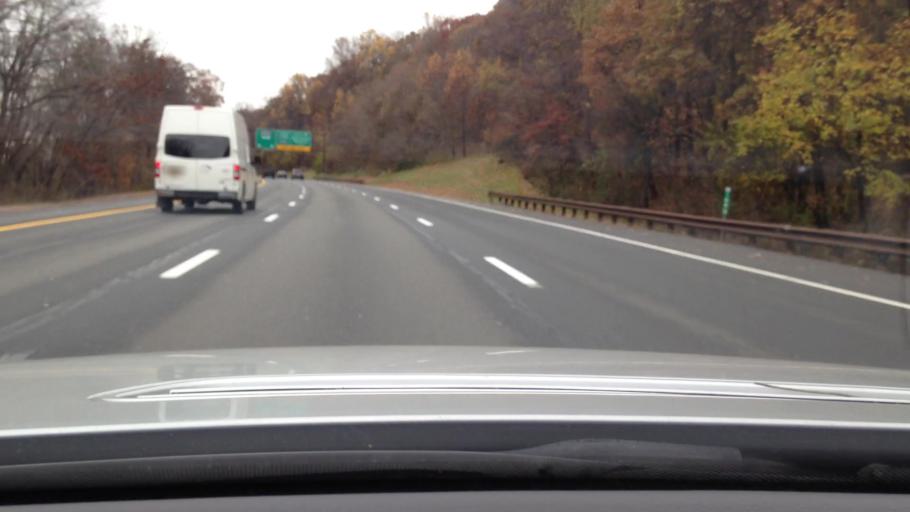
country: US
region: New Jersey
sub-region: Bergen County
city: Ho-Ho-Kus
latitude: 40.9922
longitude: -74.0736
